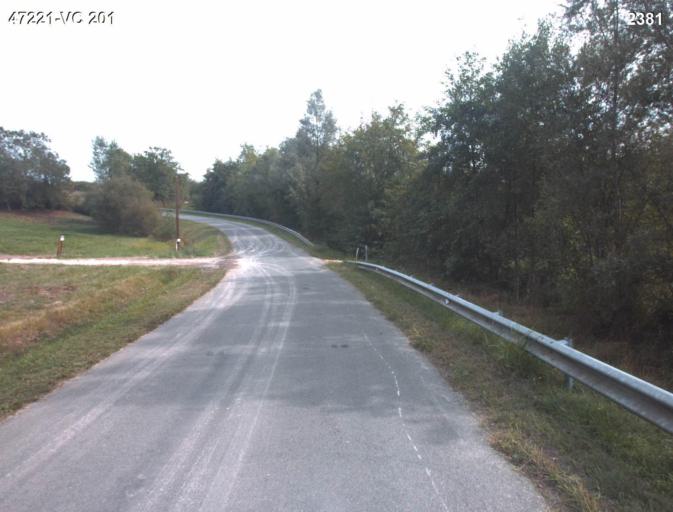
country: FR
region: Aquitaine
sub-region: Departement du Lot-et-Garonne
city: Mezin
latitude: 44.1089
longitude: 0.2472
